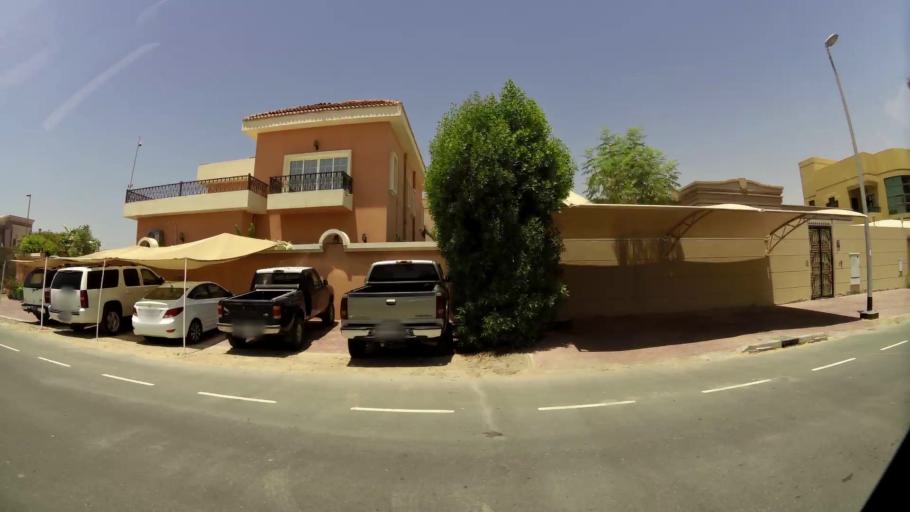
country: AE
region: Dubai
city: Dubai
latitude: 25.0964
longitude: 55.1980
